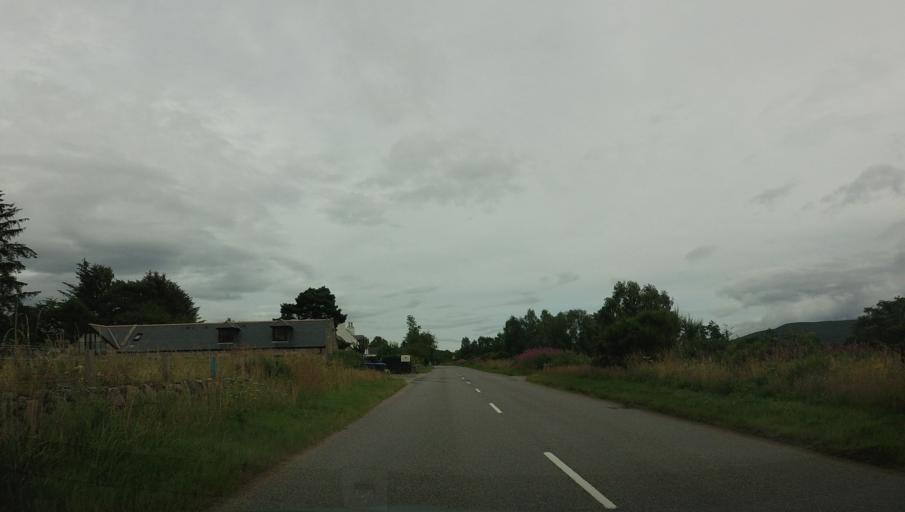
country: GB
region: Scotland
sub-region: Aberdeenshire
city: Aboyne
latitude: 57.0778
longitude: -2.8231
